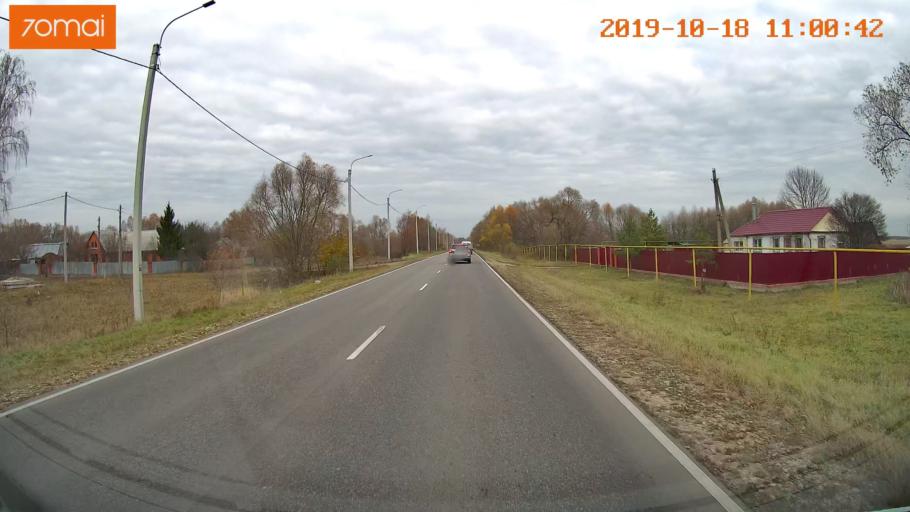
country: RU
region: Tula
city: Yepifan'
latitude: 53.8463
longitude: 38.5527
